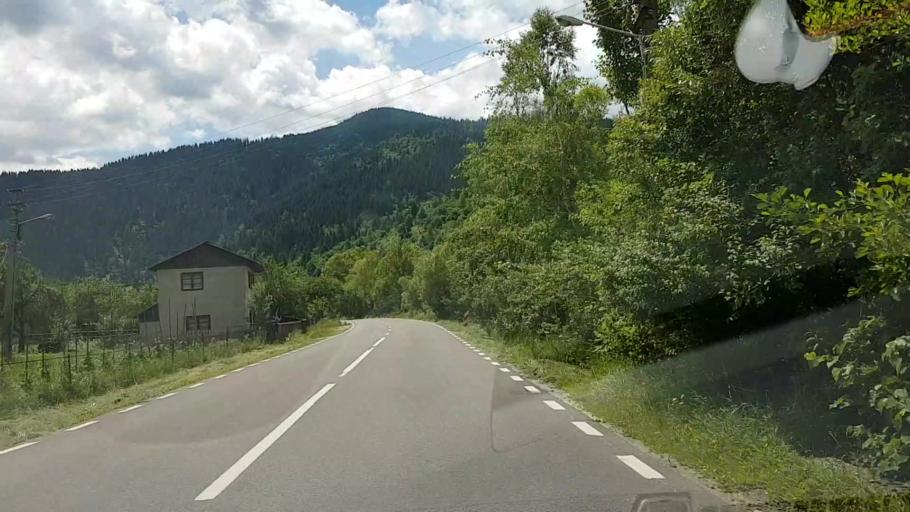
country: RO
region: Suceava
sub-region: Comuna Brosteni
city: Brosteni
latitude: 47.2510
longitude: 25.6948
